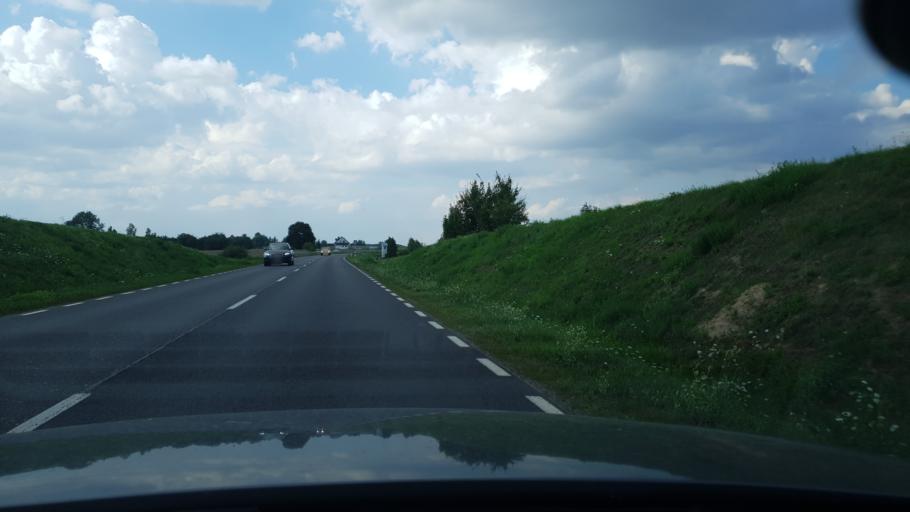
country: PL
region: Kujawsko-Pomorskie
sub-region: Powiat wabrzeski
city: Wabrzezno
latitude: 53.2914
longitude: 18.9263
